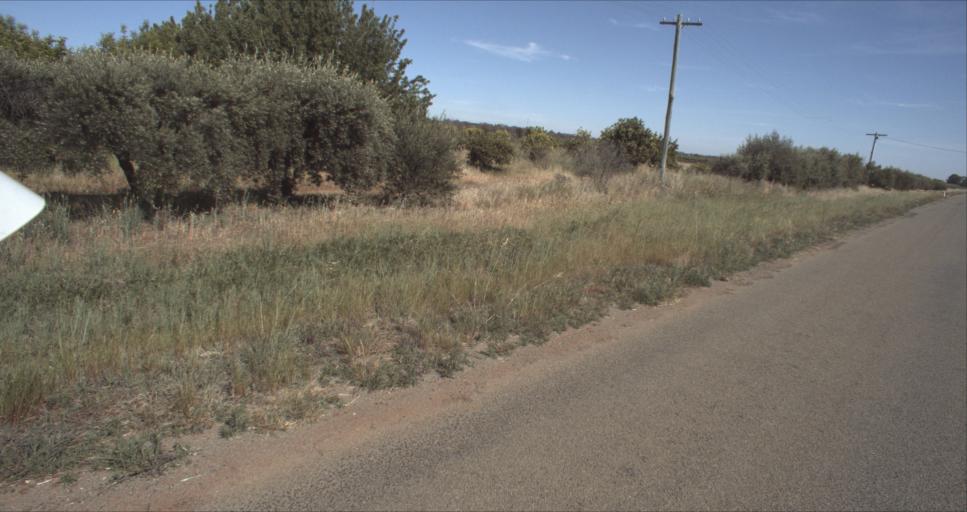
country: AU
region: New South Wales
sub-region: Leeton
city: Leeton
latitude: -34.5724
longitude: 146.4750
